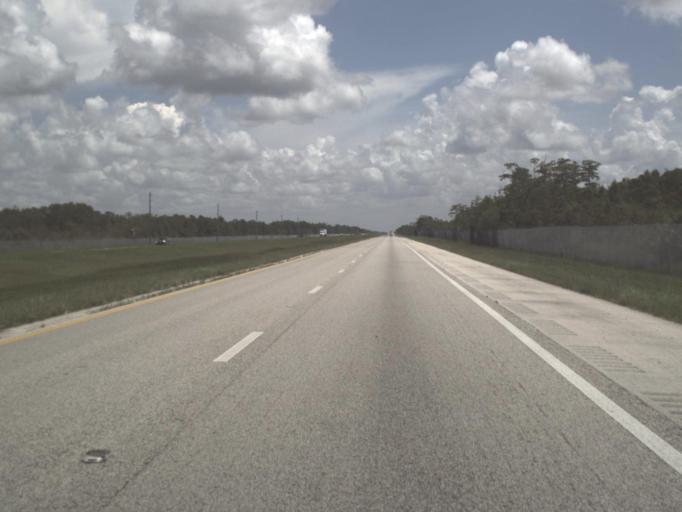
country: US
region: Florida
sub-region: Collier County
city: Immokalee
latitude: 26.1692
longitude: -81.0333
